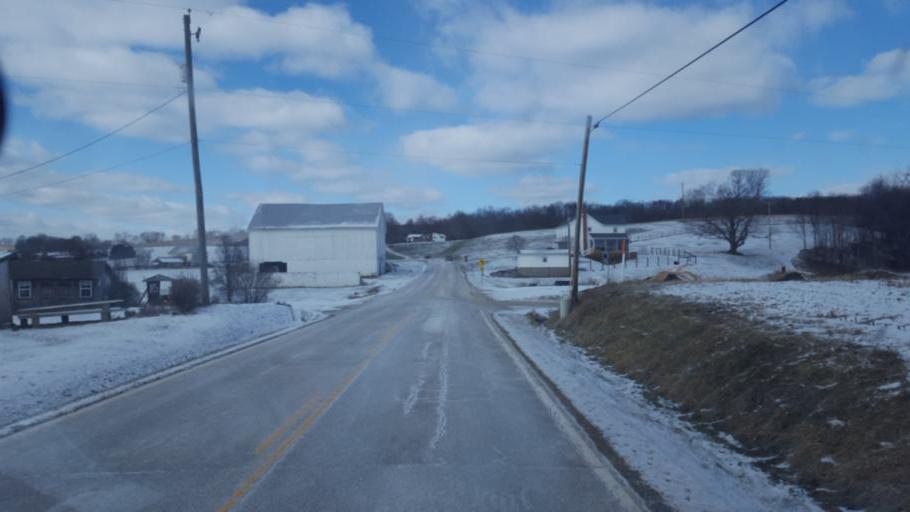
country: US
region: Ohio
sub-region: Coshocton County
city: West Lafayette
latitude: 40.3194
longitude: -81.8051
